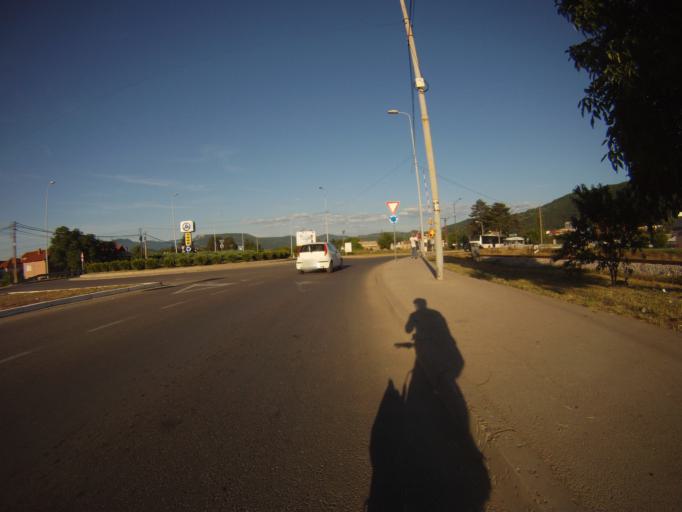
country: RS
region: Central Serbia
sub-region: Nisavski Okrug
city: Niska Banja
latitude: 43.3003
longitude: 21.9985
